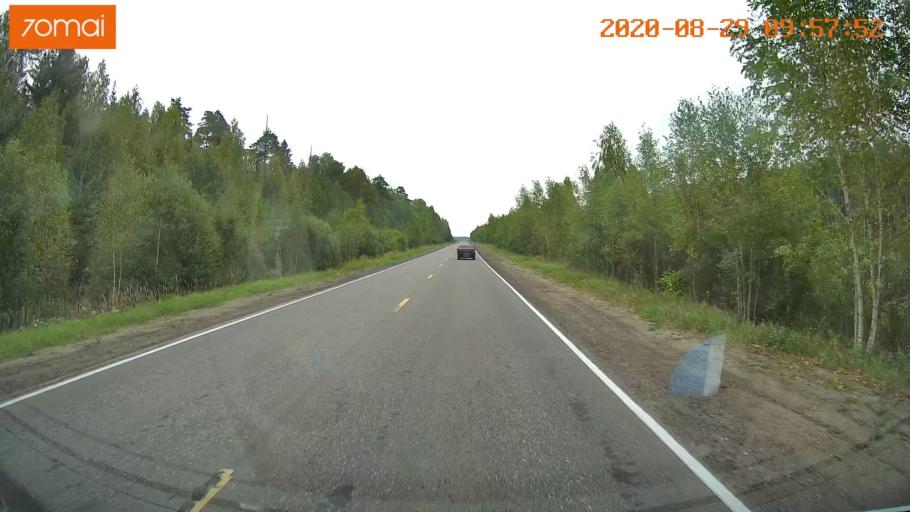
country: RU
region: Ivanovo
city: Zarechnyy
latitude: 57.4150
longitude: 42.3246
